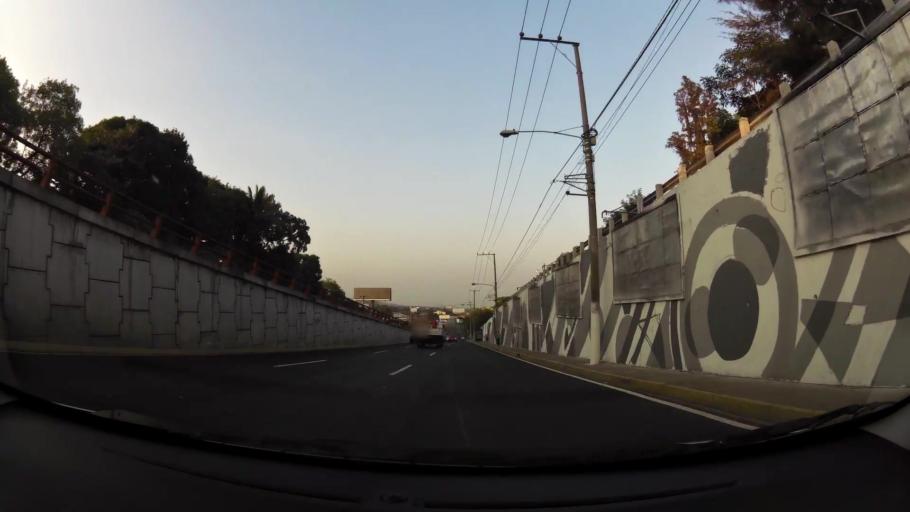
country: SV
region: San Salvador
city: San Salvador
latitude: 13.6871
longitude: -89.2175
